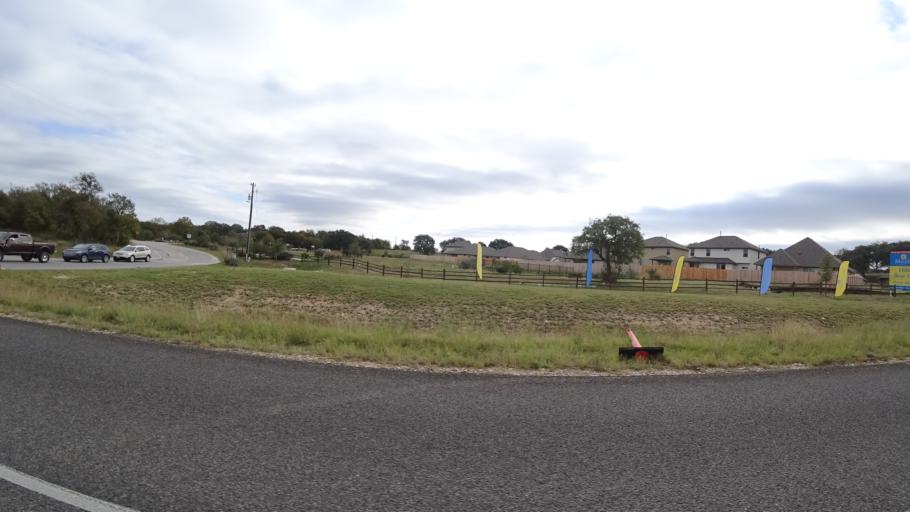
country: US
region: Texas
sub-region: Travis County
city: Manchaca
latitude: 30.1382
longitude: -97.8493
